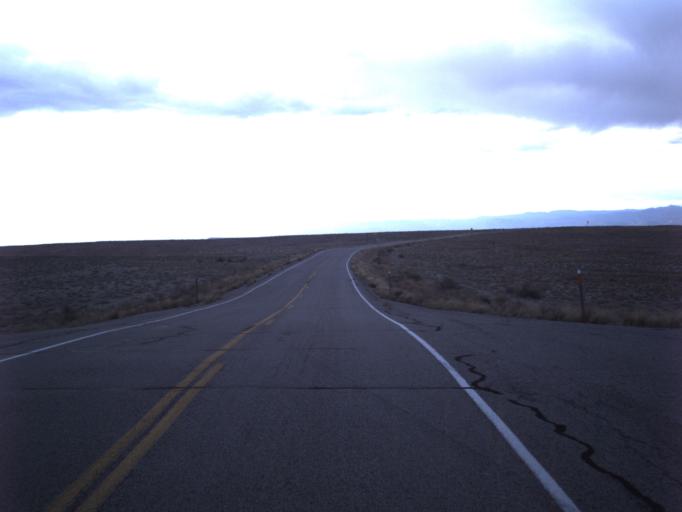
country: US
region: Utah
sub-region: Grand County
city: Moab
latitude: 38.9040
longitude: -109.3200
